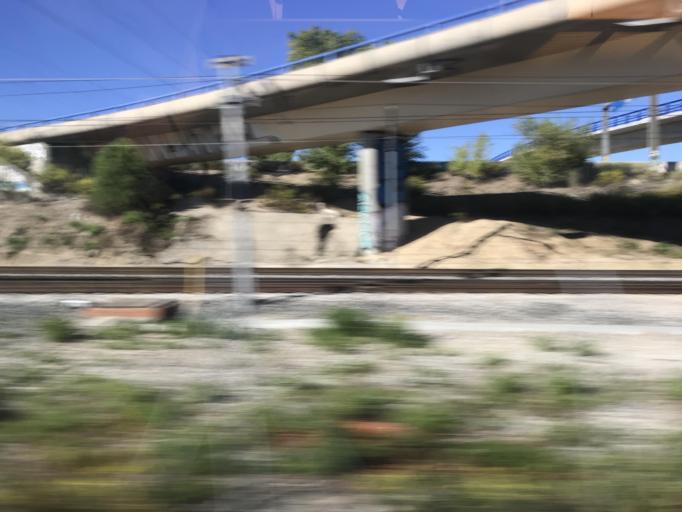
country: ES
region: Madrid
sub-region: Provincia de Madrid
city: Las Tablas
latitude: 40.5183
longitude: -3.6842
